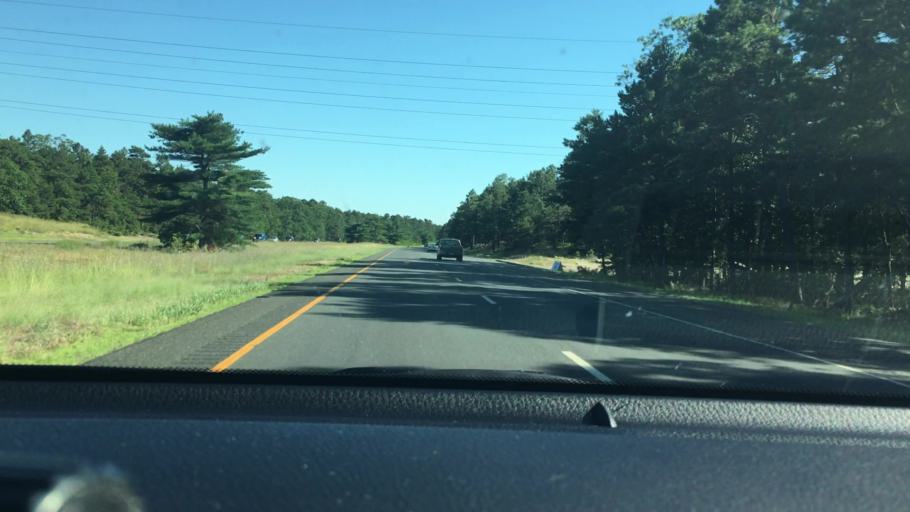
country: US
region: New Jersey
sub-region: Gloucester County
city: Newfield
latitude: 39.5376
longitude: -75.0632
